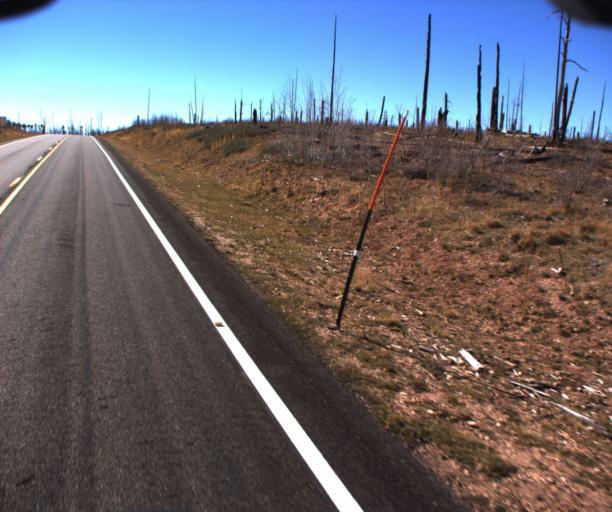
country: US
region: Arizona
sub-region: Coconino County
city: Fredonia
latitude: 36.5779
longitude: -112.1755
